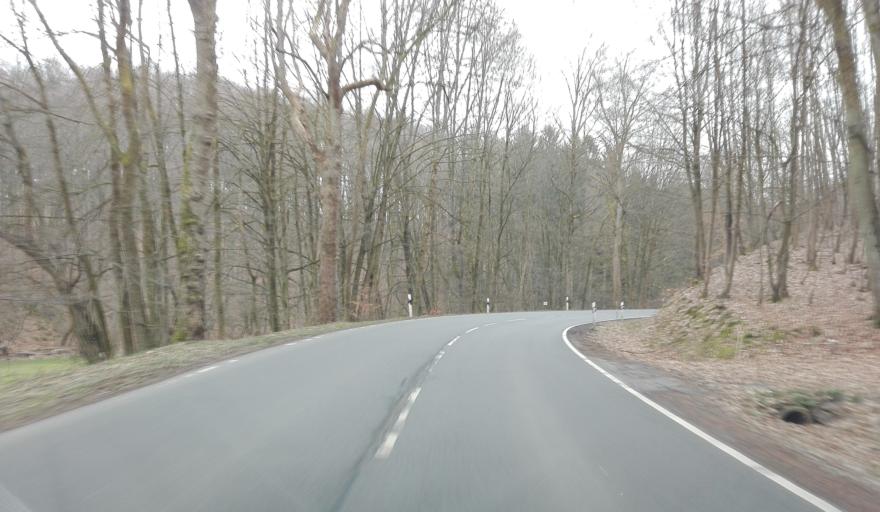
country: DE
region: Hesse
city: Lutzelbach
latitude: 49.7610
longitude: 8.7240
